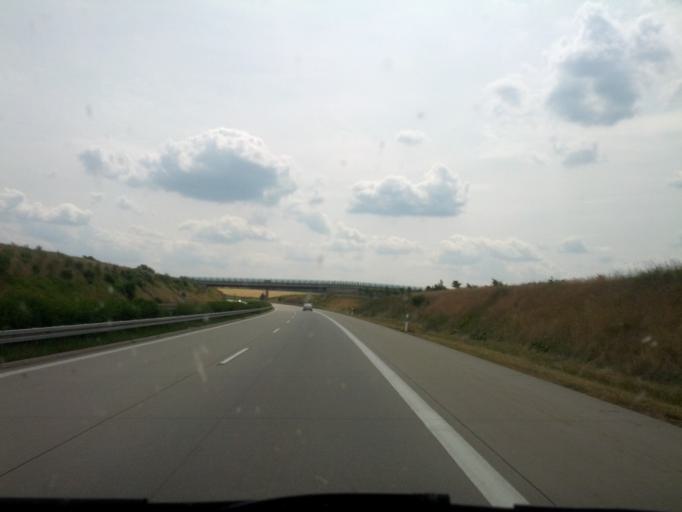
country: DE
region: Saxony
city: Liebstadt
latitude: 50.8102
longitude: 13.8816
